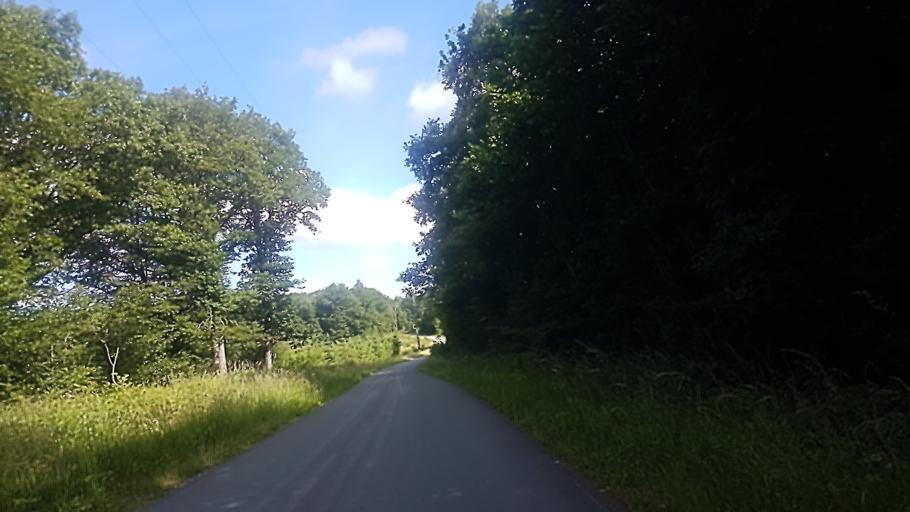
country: BE
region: Wallonia
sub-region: Province de Namur
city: Couvin
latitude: 50.0462
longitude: 4.5619
